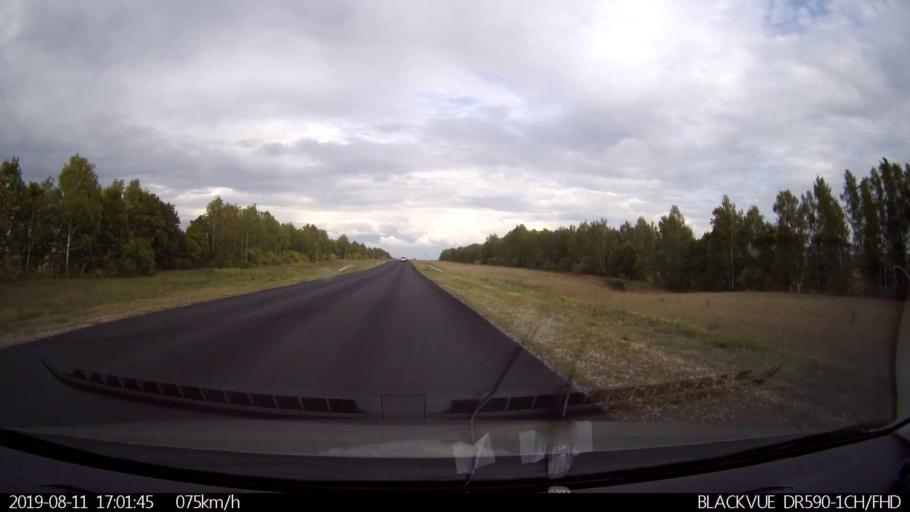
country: RU
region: Ulyanovsk
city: Mayna
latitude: 54.3074
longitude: 47.7033
